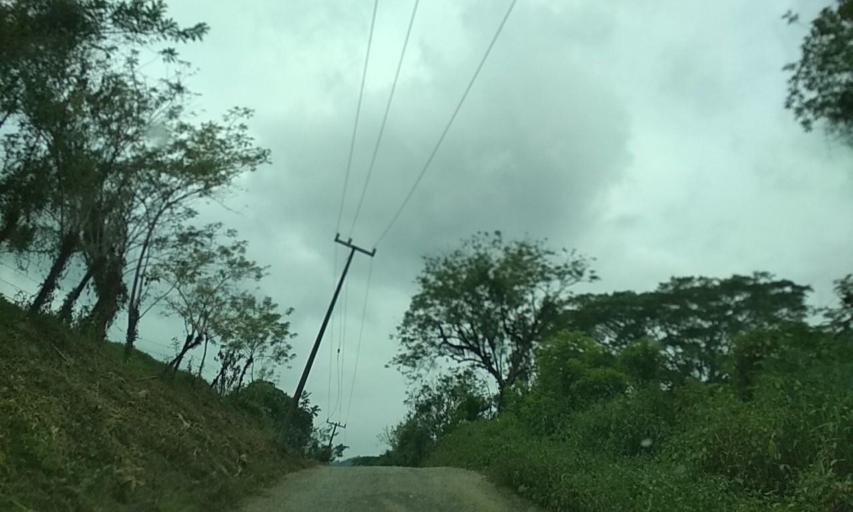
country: MX
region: Veracruz
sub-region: Uxpanapa
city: Poblado 10
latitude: 17.4931
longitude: -94.1314
